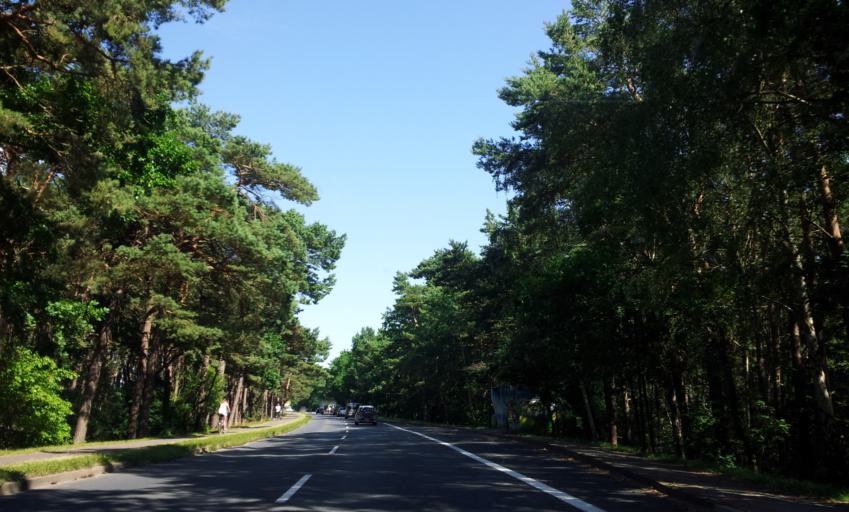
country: DE
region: Mecklenburg-Vorpommern
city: Glowe
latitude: 54.5691
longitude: 13.4549
